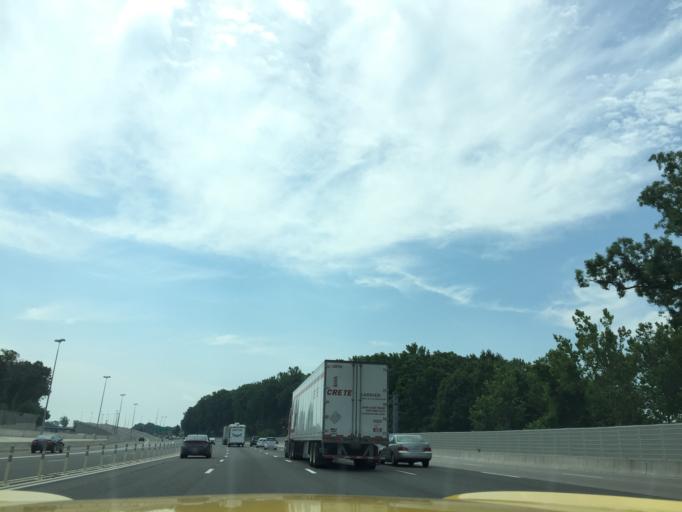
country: US
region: Virginia
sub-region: Fairfax County
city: Ravensworth
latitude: 38.8187
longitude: -77.2223
